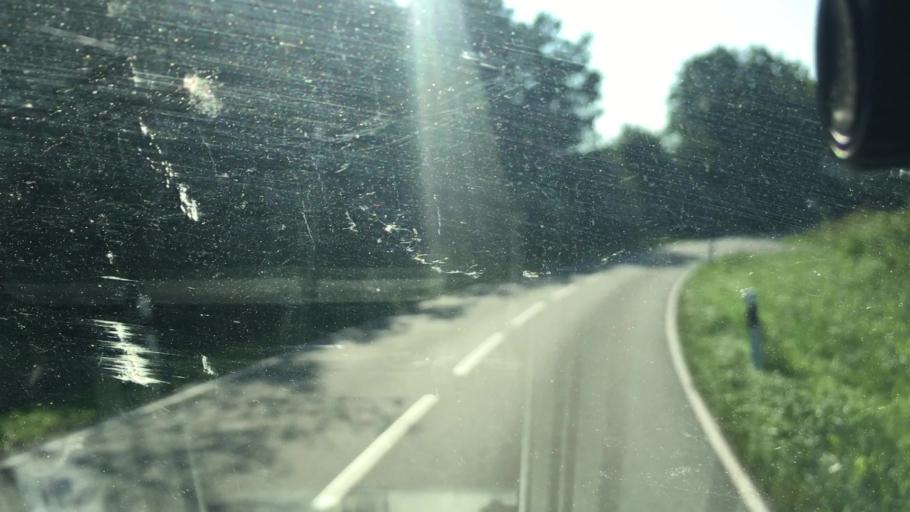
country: DE
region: Lower Saxony
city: Wittmund
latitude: 53.6375
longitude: 7.8284
